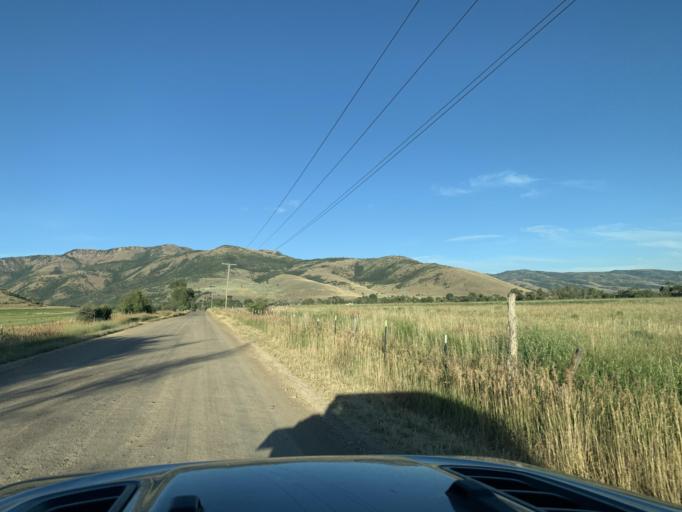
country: US
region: Utah
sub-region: Weber County
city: Wolf Creek
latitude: 41.2931
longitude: -111.7710
